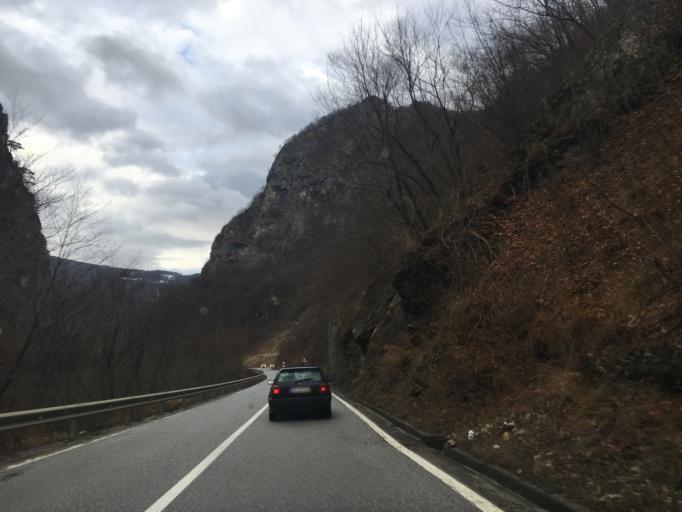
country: RS
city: Sokolovo Brdo
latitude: 43.1633
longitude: 19.7705
